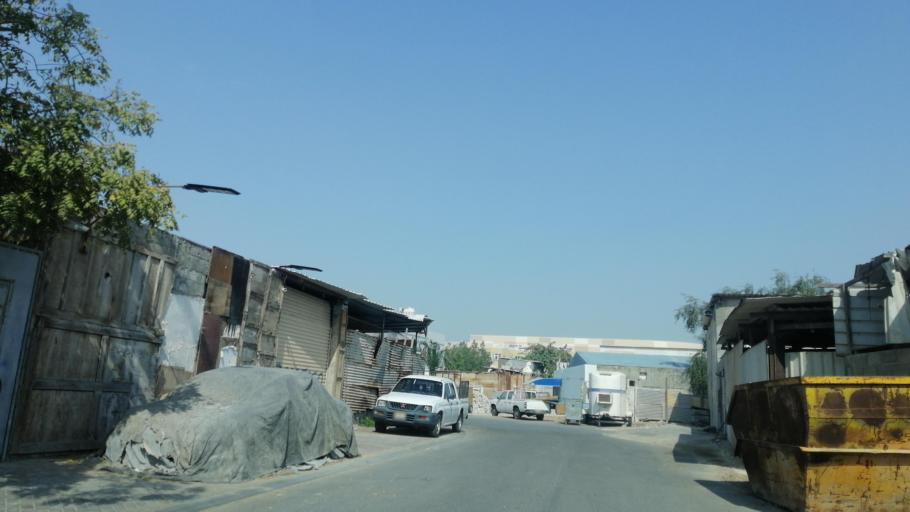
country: BH
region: Muharraq
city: Al Muharraq
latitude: 26.2525
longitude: 50.6293
